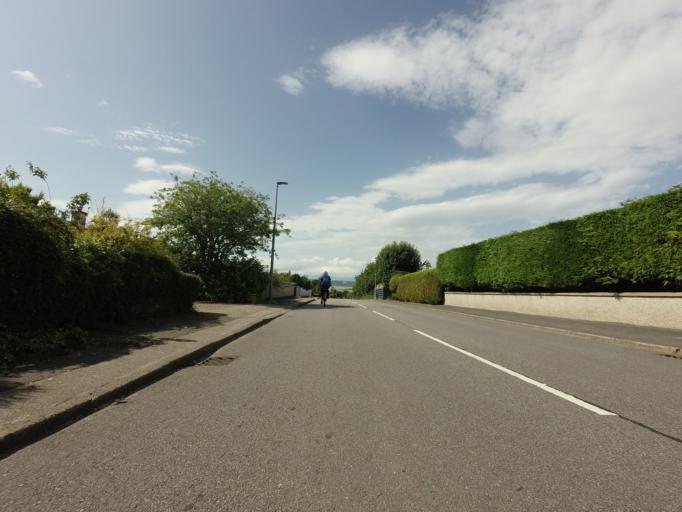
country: GB
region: Scotland
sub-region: Highland
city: Fortrose
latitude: 57.4932
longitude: -4.1112
